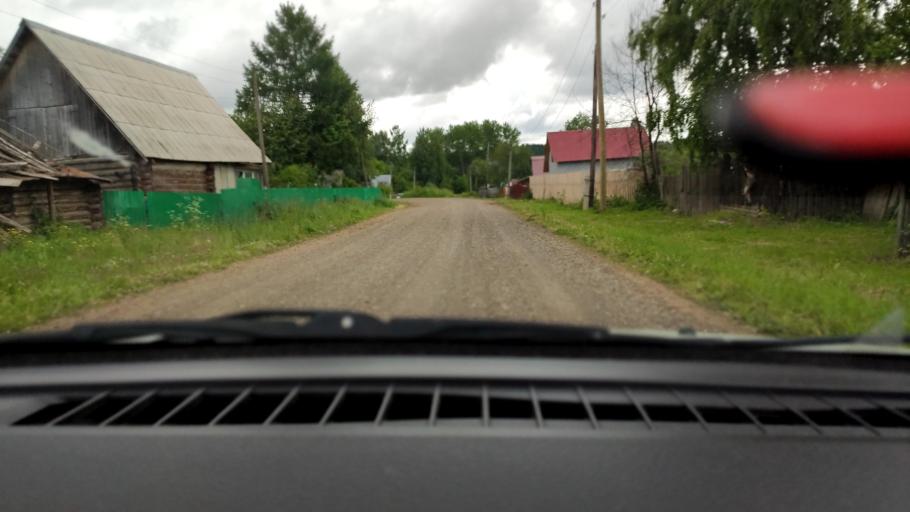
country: RU
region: Perm
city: Chaykovskaya
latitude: 58.1314
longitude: 55.5547
